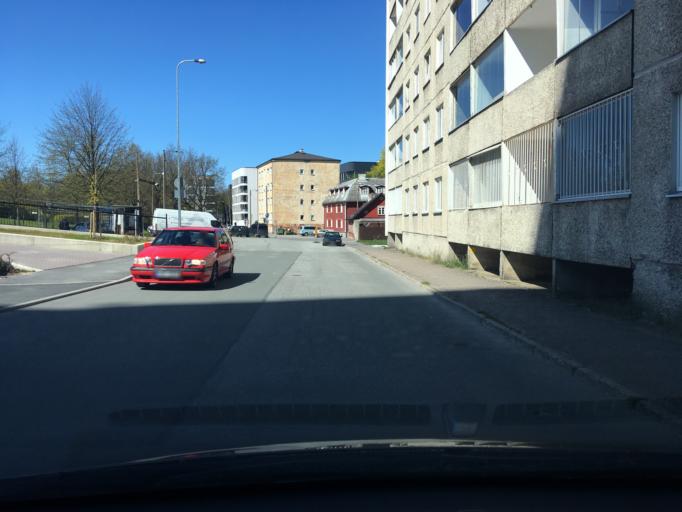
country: EE
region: Harju
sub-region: Tallinna linn
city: Tallinn
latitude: 59.4267
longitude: 24.7672
